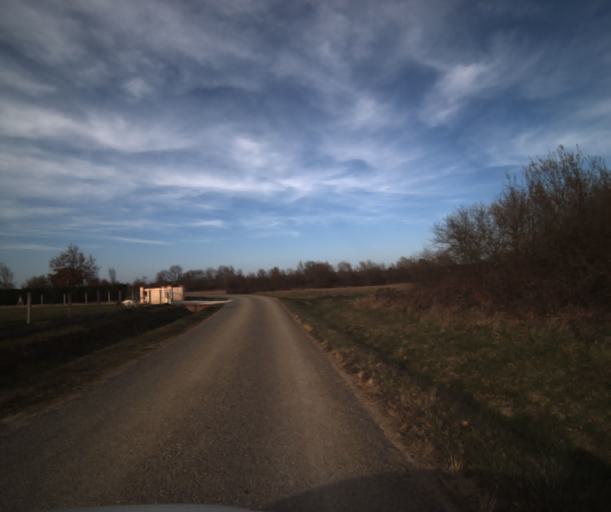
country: FR
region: Midi-Pyrenees
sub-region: Departement du Tarn-et-Garonne
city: Labastide-Saint-Pierre
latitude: 43.9100
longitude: 1.3748
